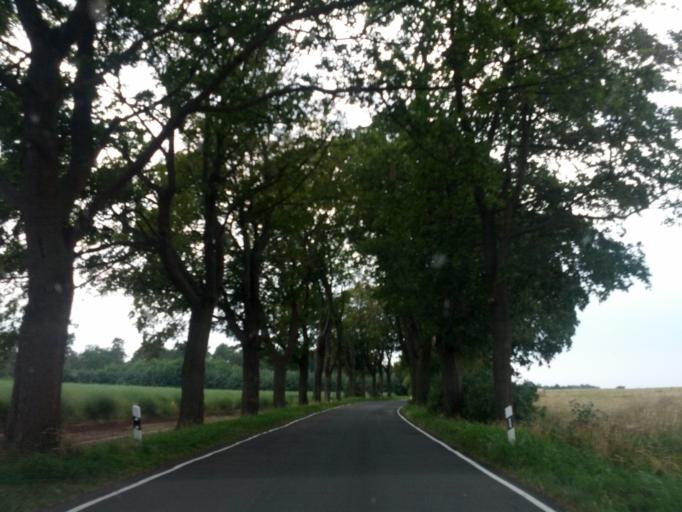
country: DE
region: Brandenburg
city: Kremmen
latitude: 52.7456
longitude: 12.9349
